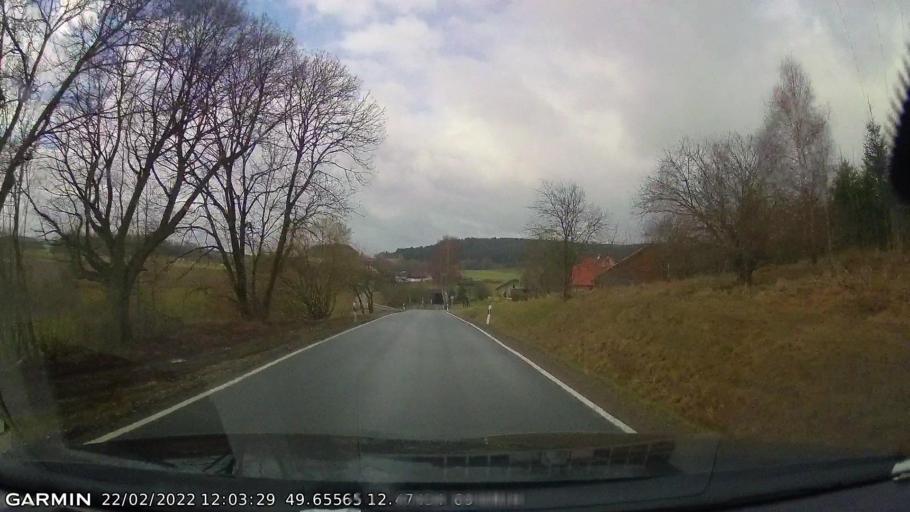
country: DE
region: Bavaria
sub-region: Upper Palatinate
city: Waidhaus
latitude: 49.6557
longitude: 12.4742
